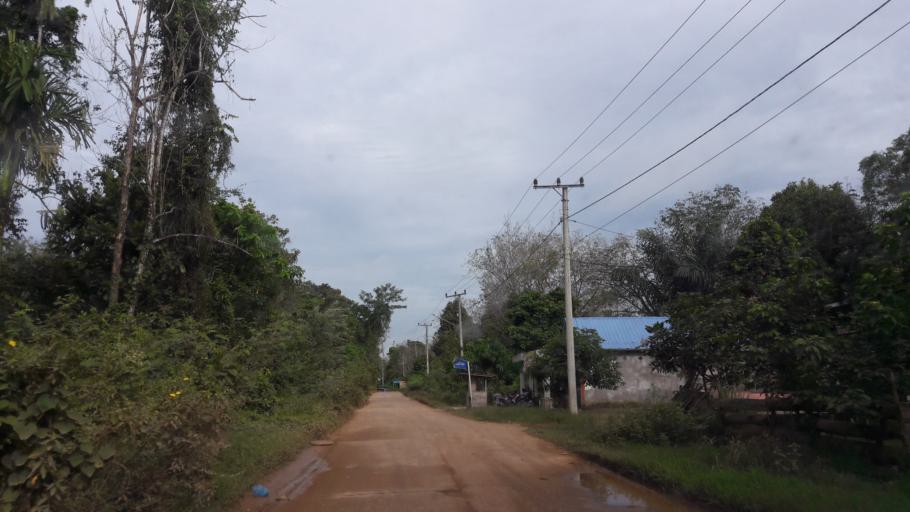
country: ID
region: South Sumatra
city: Gunungmegang Dalam
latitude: -3.2863
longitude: 103.7246
